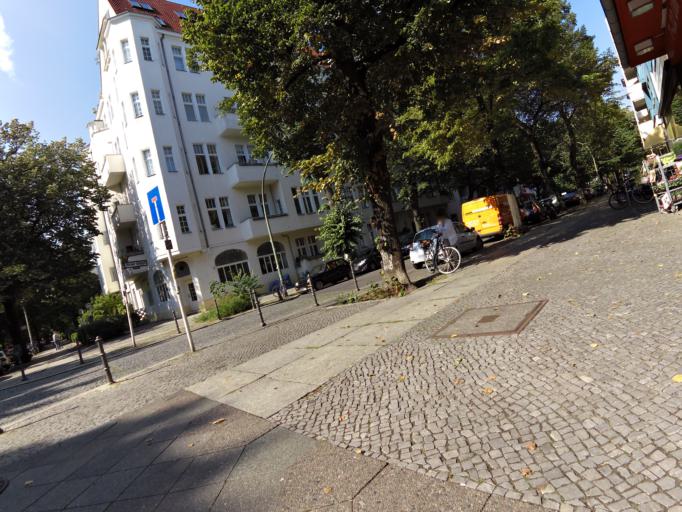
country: DE
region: Berlin
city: Berlin Schoeneberg
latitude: 52.4907
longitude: 13.3357
